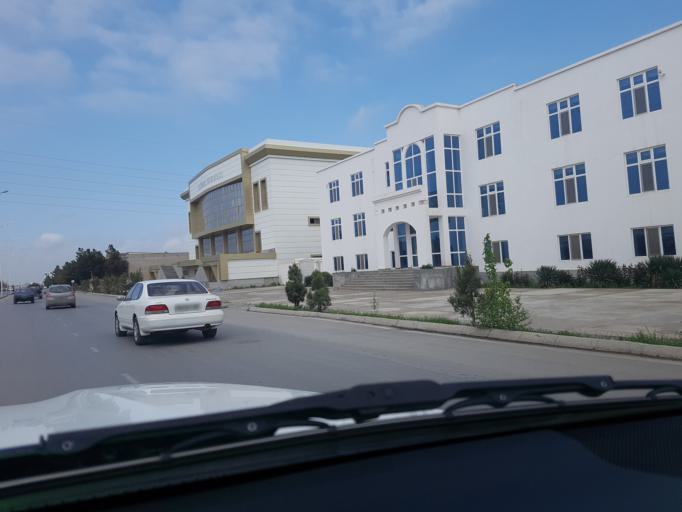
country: TM
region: Lebap
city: Turkmenabat
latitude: 39.0726
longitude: 63.5927
